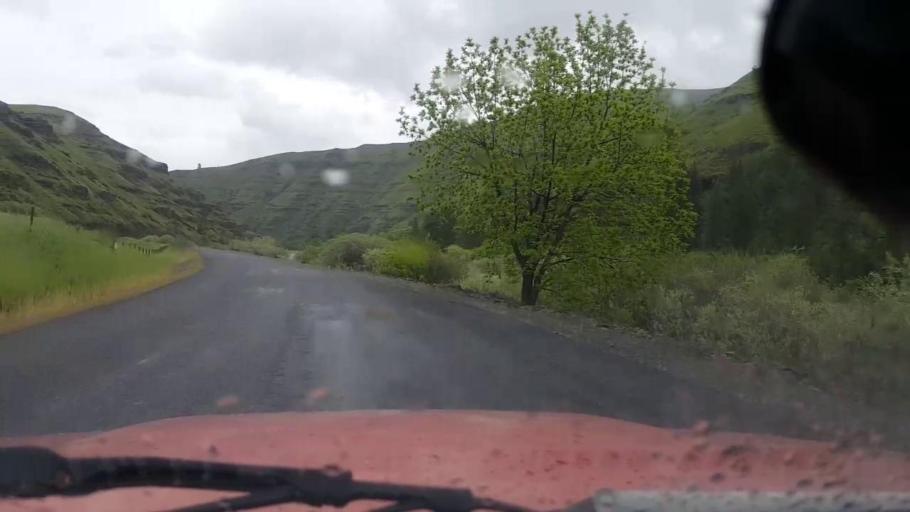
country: US
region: Washington
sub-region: Asotin County
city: Asotin
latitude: 46.0276
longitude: -117.3106
